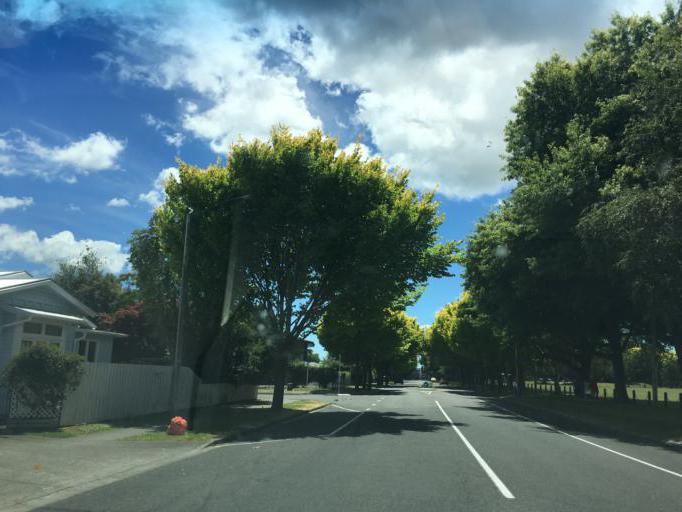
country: NZ
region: Hawke's Bay
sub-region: Hastings District
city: Hastings
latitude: -39.6441
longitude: 176.8599
